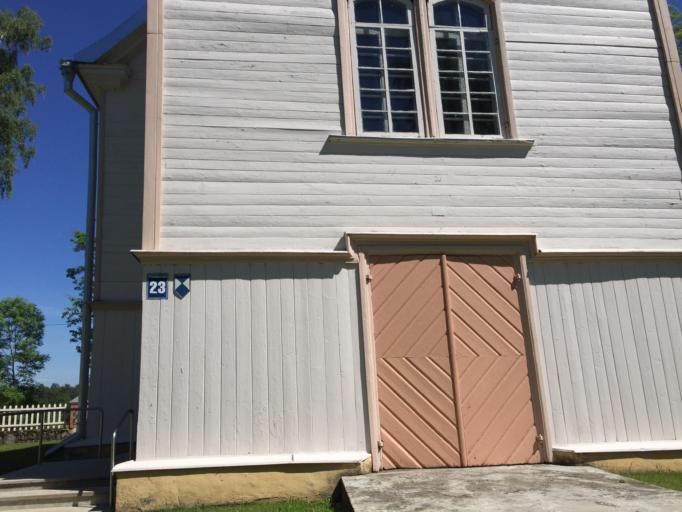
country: LV
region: Preilu Rajons
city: Jaunaglona
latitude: 56.2344
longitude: 27.2308
